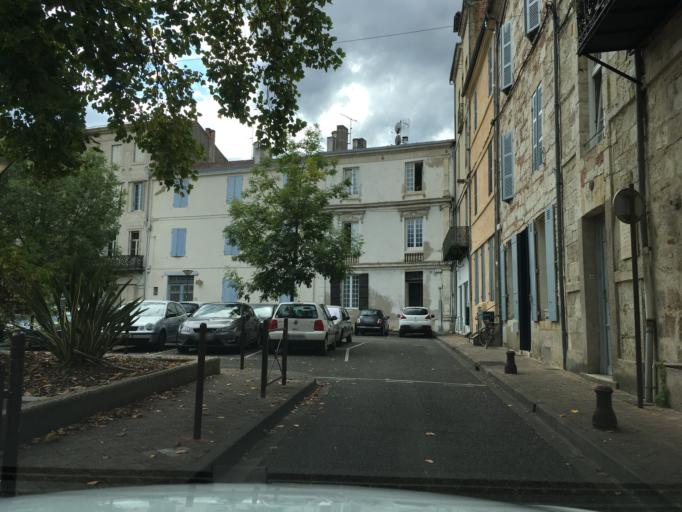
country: FR
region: Aquitaine
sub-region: Departement du Lot-et-Garonne
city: Le Passage
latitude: 44.2055
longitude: 0.6147
